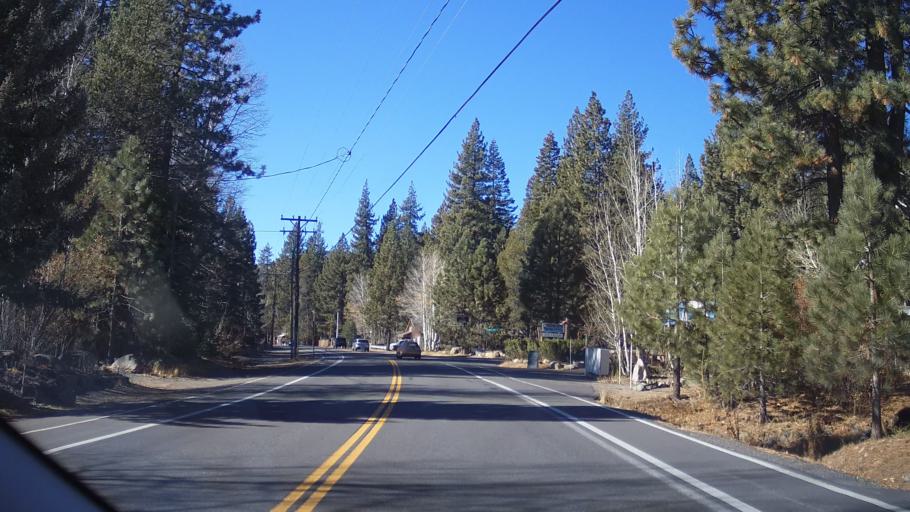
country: US
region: California
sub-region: Nevada County
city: Truckee
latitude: 39.3252
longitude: -120.2848
